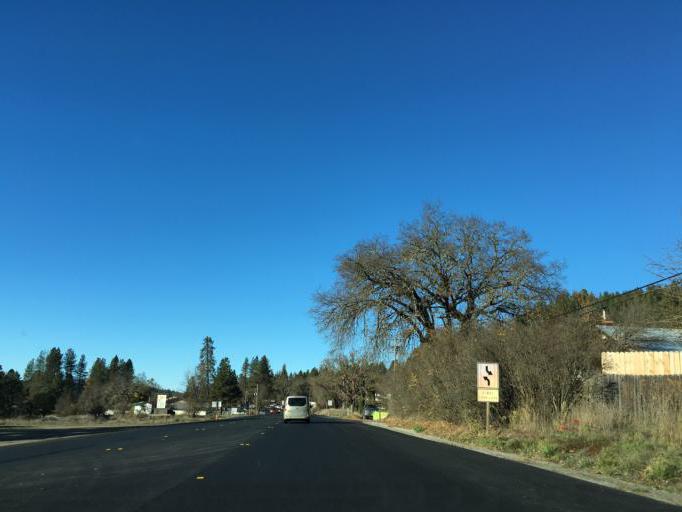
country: US
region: California
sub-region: Mendocino County
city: Laytonville
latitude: 39.6815
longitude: -123.4765
